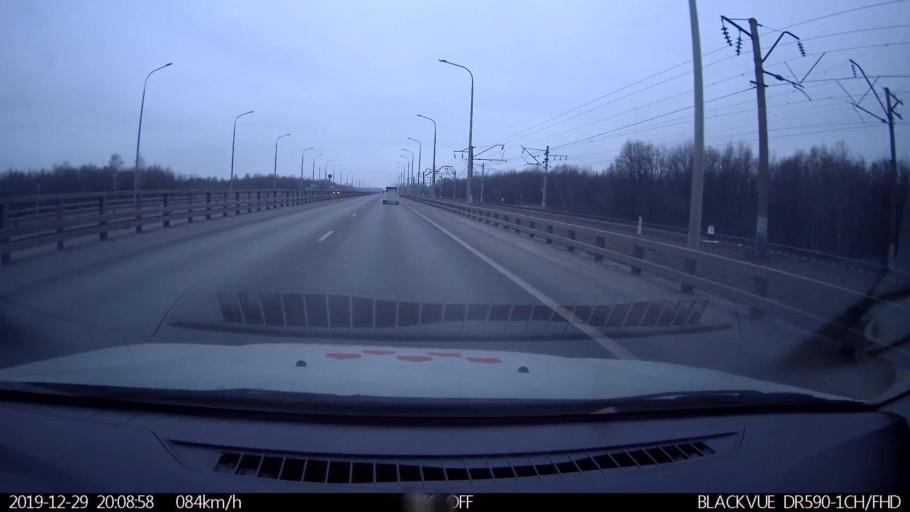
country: RU
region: Nizjnij Novgorod
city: Neklyudovo
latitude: 56.3795
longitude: 43.9571
